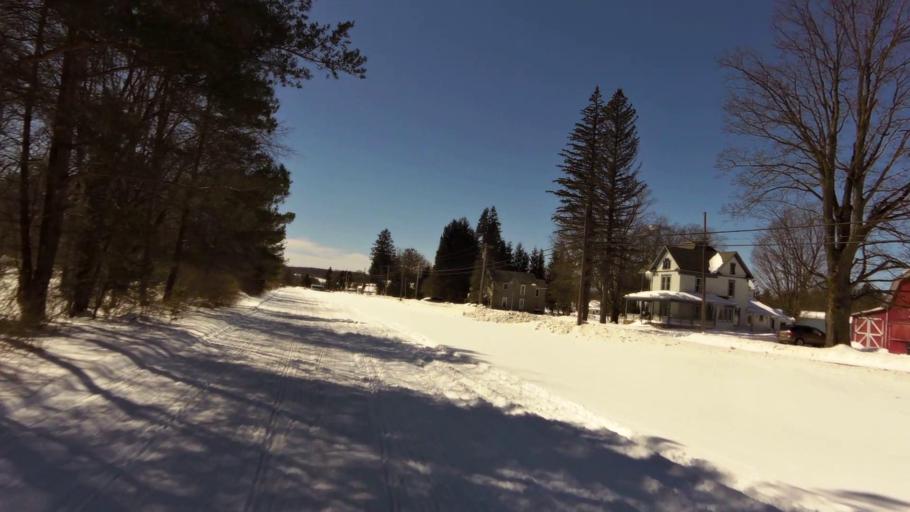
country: US
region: New York
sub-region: Wyoming County
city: Arcade
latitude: 42.4296
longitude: -78.3573
